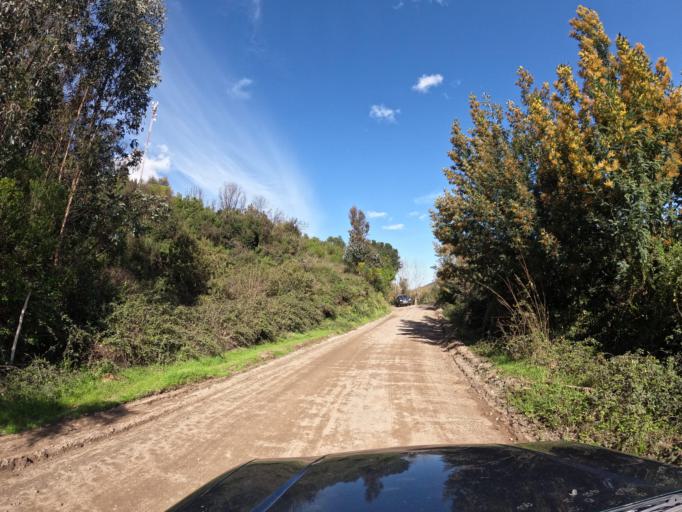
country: CL
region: Biobio
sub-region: Provincia de Concepcion
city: Chiguayante
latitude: -37.0641
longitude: -72.8823
